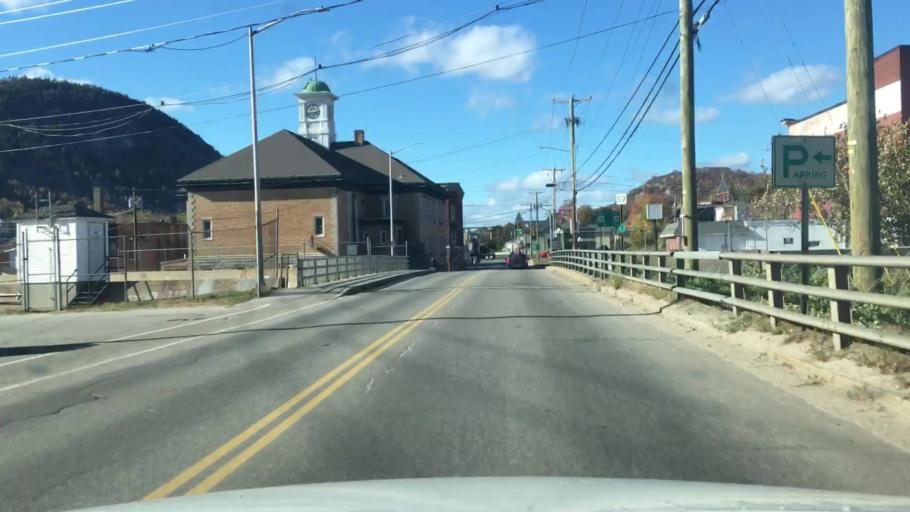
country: US
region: New Hampshire
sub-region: Coos County
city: Berlin
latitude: 44.4694
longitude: -71.1788
